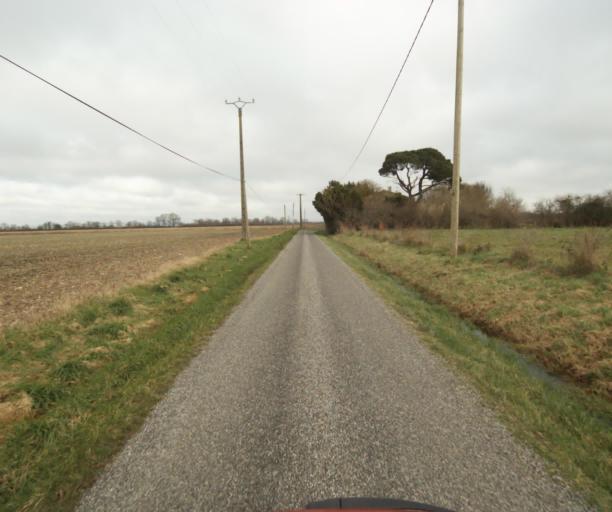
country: FR
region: Midi-Pyrenees
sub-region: Departement de l'Ariege
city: Mazeres
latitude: 43.1844
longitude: 1.6679
